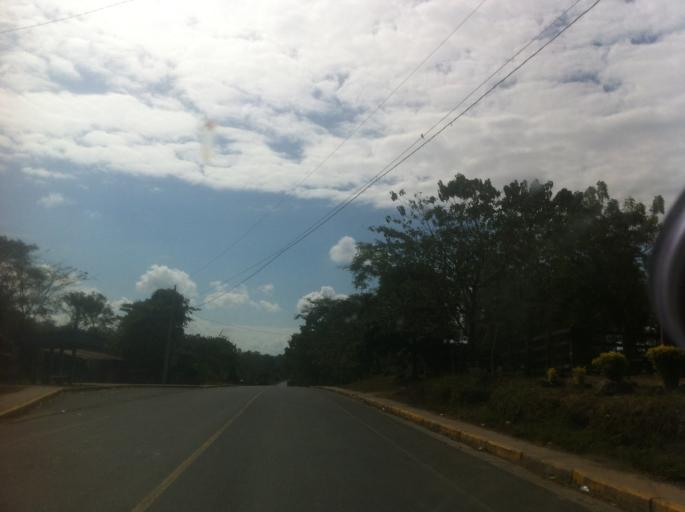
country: NI
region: Rio San Juan
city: San Carlos
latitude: 11.2841
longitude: -84.7193
